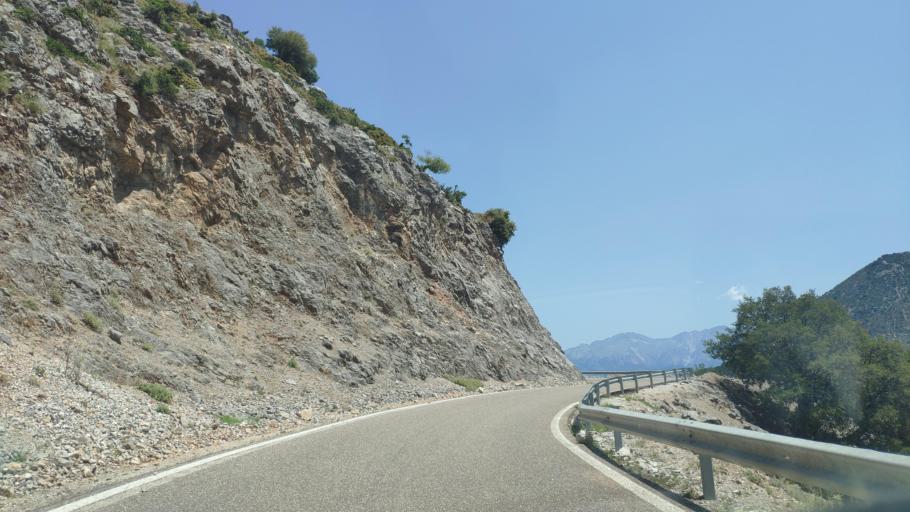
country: GR
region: West Greece
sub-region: Nomos Aitolias kai Akarnanias
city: Krikellos
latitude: 39.0221
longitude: 21.3699
